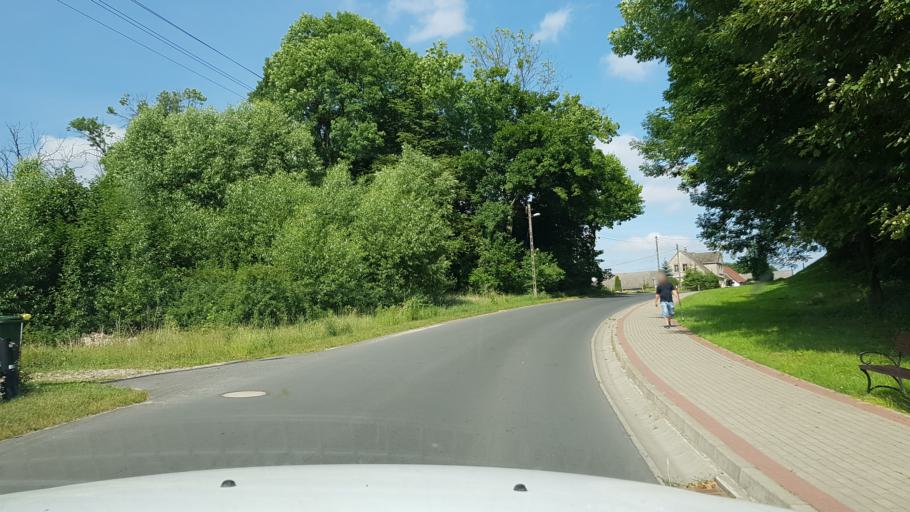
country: PL
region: West Pomeranian Voivodeship
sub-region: Powiat goleniowski
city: Osina
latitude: 53.6038
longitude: 15.0082
